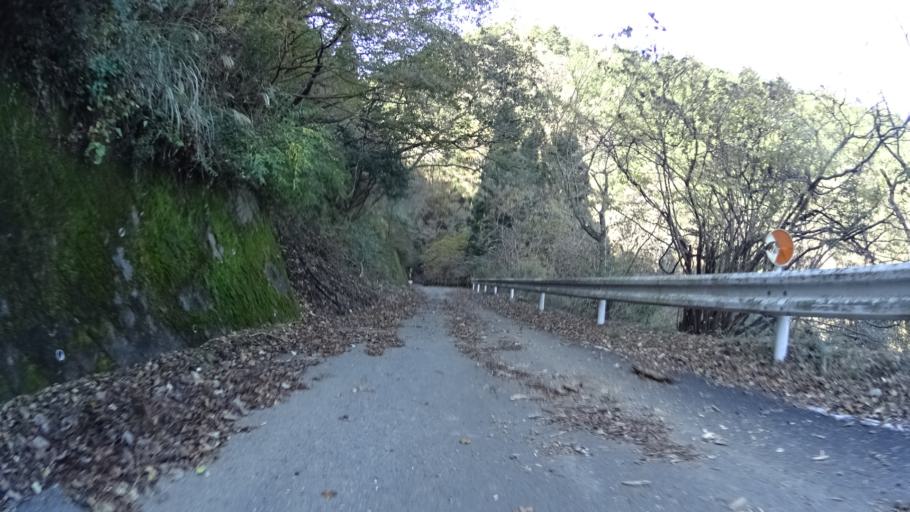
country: JP
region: Kanagawa
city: Atsugi
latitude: 35.5089
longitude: 139.2676
